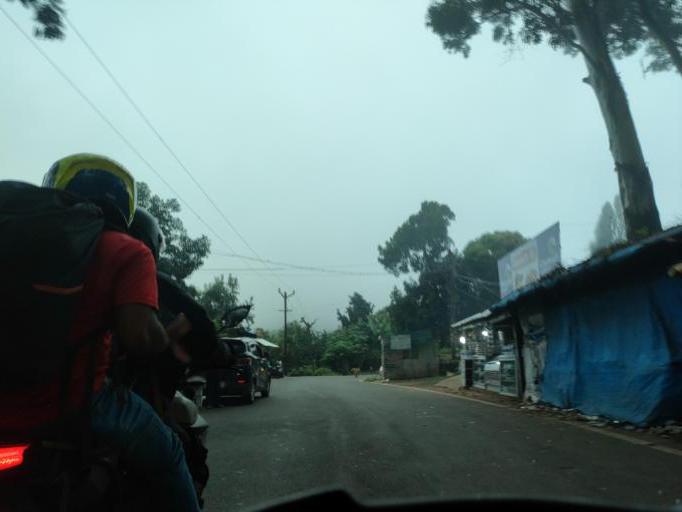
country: IN
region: Tamil Nadu
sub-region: Dindigul
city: Ayakudi
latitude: 10.3388
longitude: 77.5642
